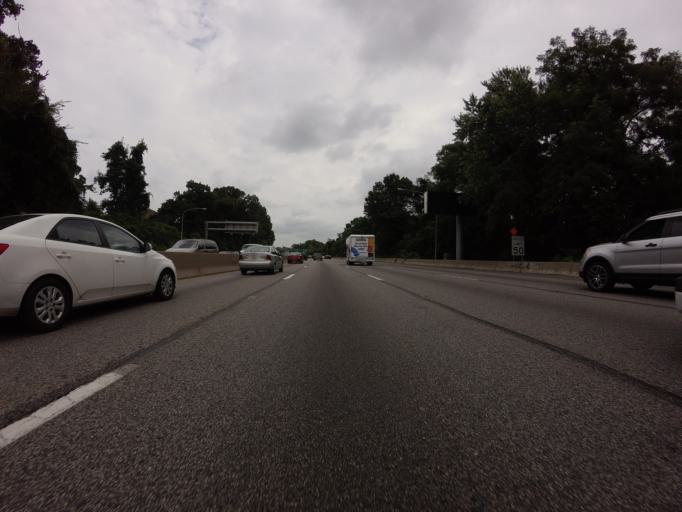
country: US
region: Pennsylvania
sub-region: Montgomery County
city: Bala-Cynwyd
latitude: 39.9922
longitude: -75.2017
